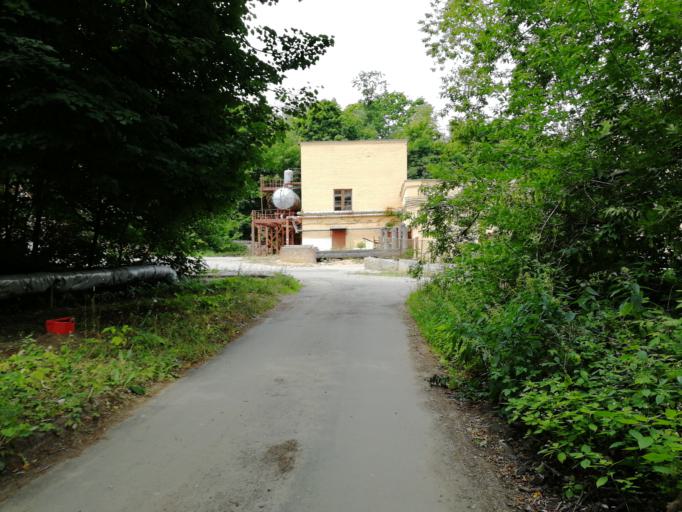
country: RU
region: Tula
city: Tula
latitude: 54.1809
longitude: 37.5974
